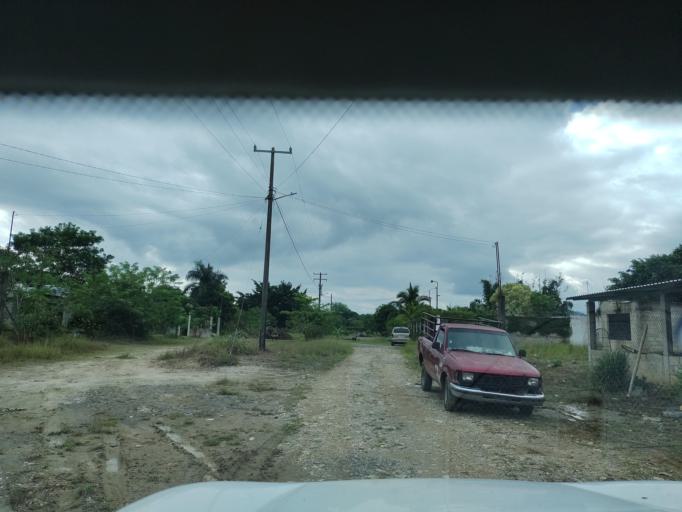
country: MX
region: Veracruz
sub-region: Atzalan
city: Colonias Pedernales
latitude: 20.0385
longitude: -97.0724
